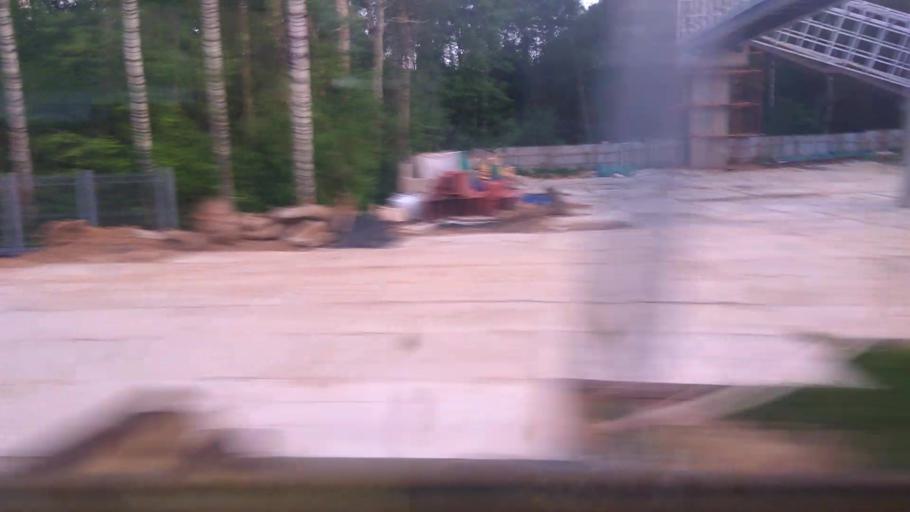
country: RU
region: Moskovskaya
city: Korolev
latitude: 55.9261
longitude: 37.7898
